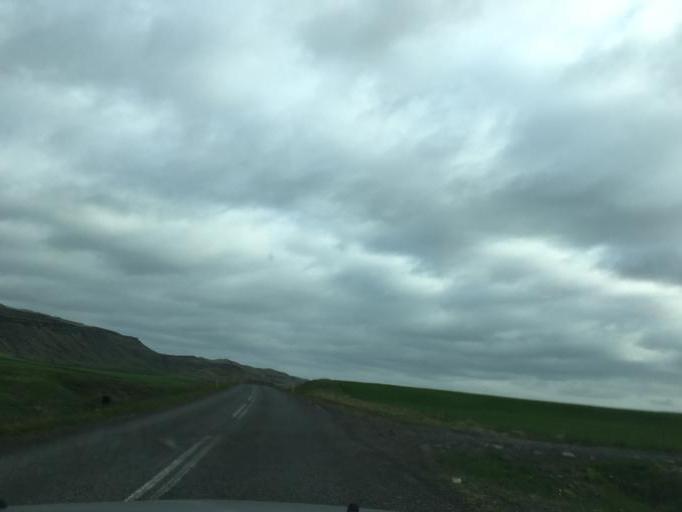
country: IS
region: South
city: Vestmannaeyjar
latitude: 64.1984
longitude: -20.2778
